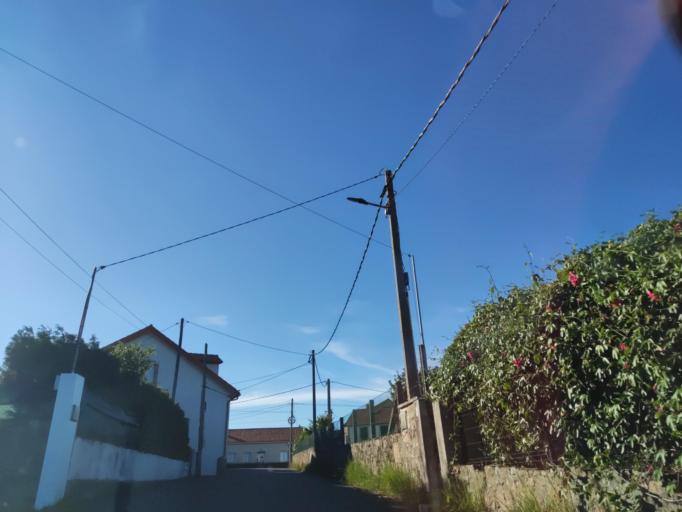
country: ES
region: Galicia
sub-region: Provincia da Coruna
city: Boiro
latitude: 42.5921
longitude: -8.9282
